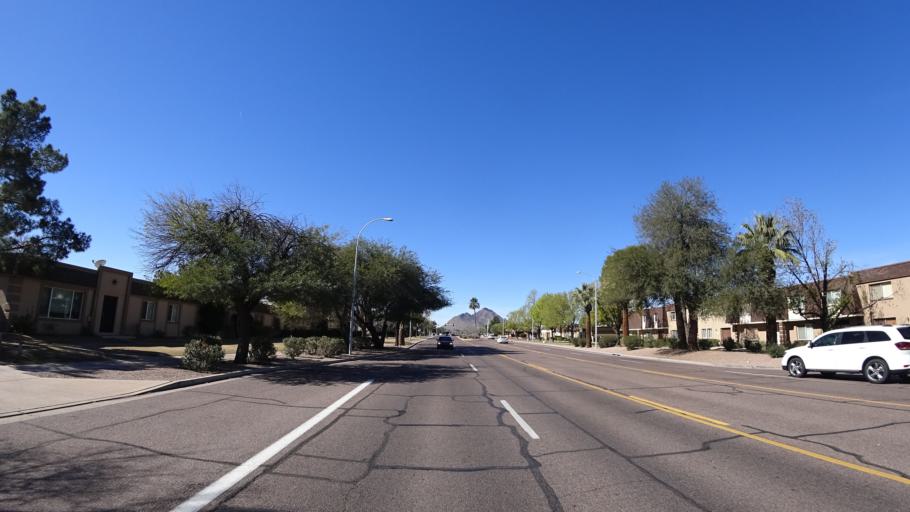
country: US
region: Arizona
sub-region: Maricopa County
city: Scottsdale
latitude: 33.5093
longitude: -111.8982
